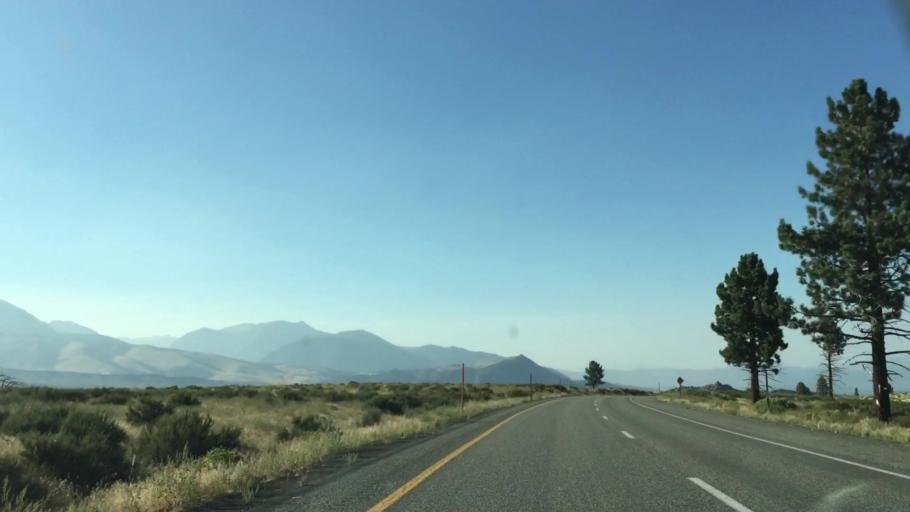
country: US
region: California
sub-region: Mono County
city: Mammoth Lakes
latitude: 37.8320
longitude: -119.0687
